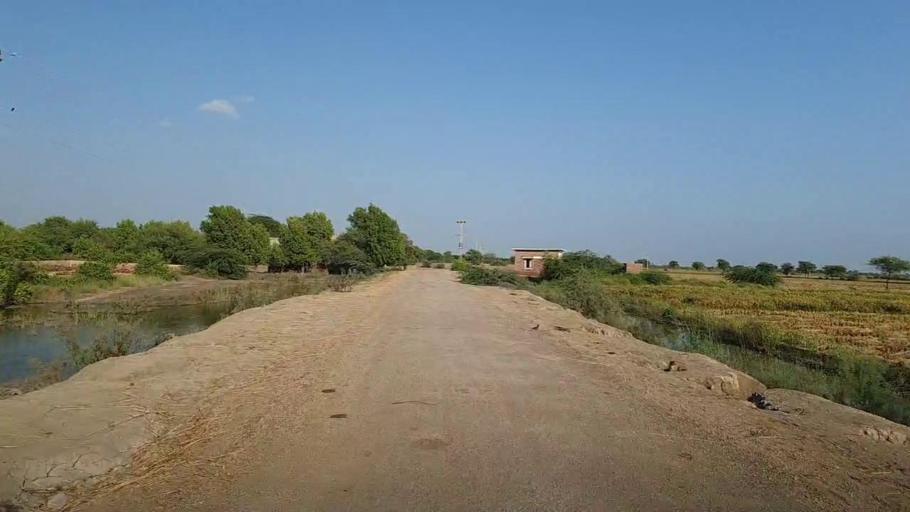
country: PK
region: Sindh
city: Kario
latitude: 24.7765
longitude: 68.6728
